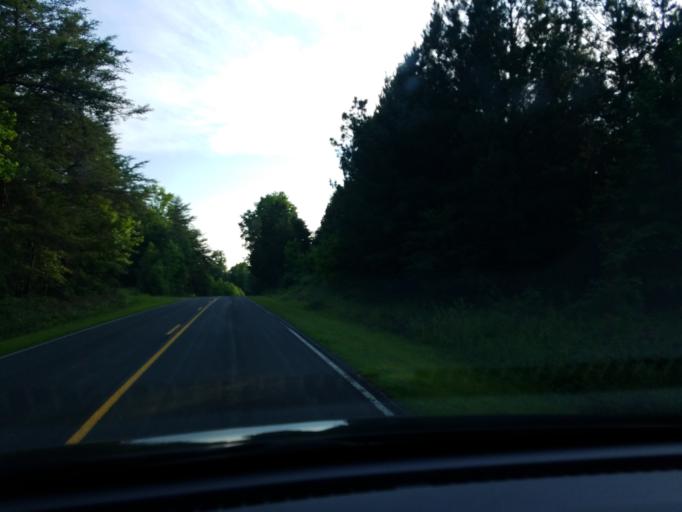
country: US
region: North Carolina
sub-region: Granville County
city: Butner
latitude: 36.1859
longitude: -78.8418
